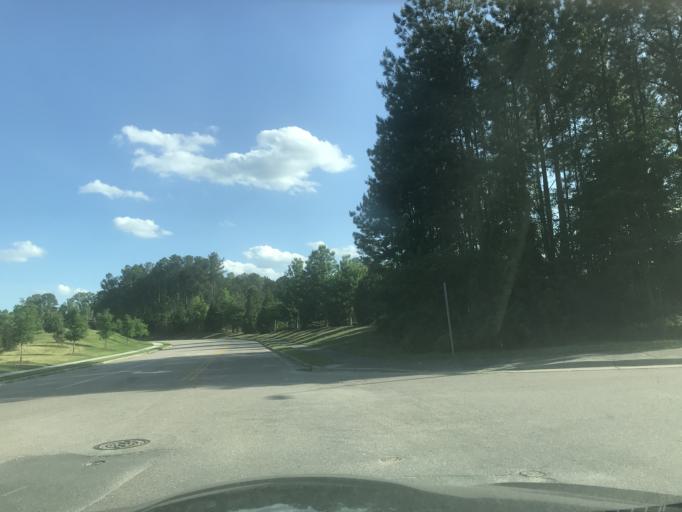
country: US
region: North Carolina
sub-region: Wake County
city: Knightdale
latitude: 35.7623
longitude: -78.4286
